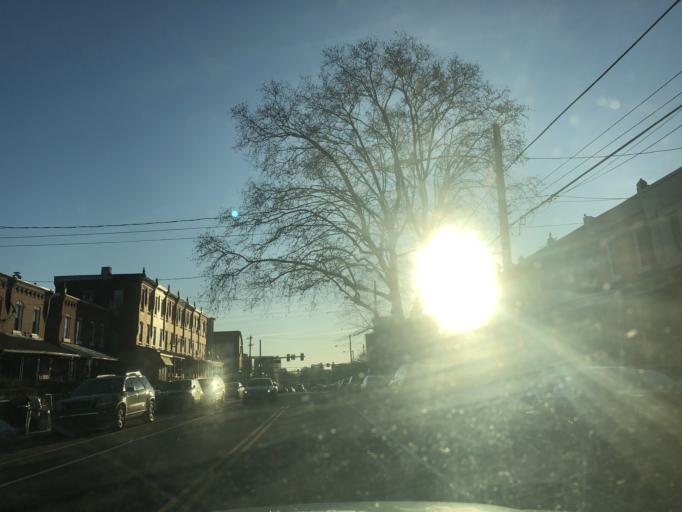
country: US
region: Pennsylvania
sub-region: Delaware County
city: Millbourne
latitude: 39.9661
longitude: -75.2276
